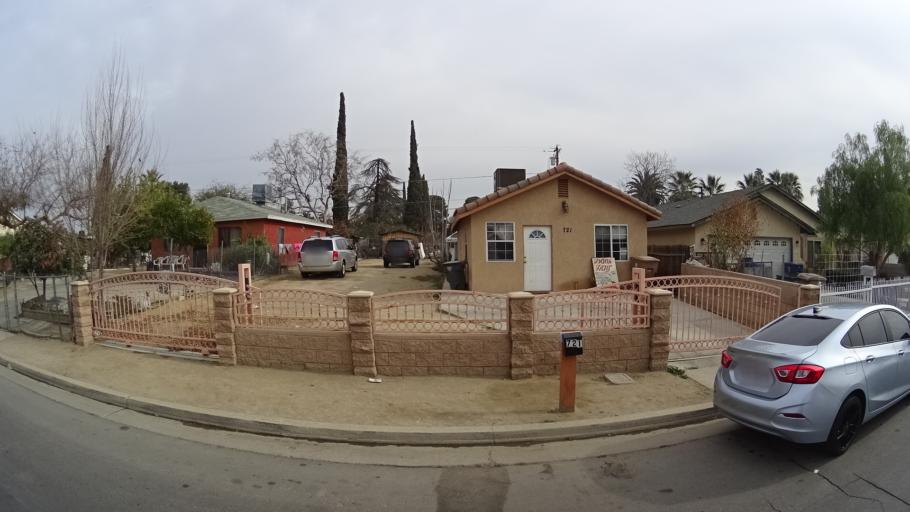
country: US
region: California
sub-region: Kern County
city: Bakersfield
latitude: 35.3639
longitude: -118.9990
